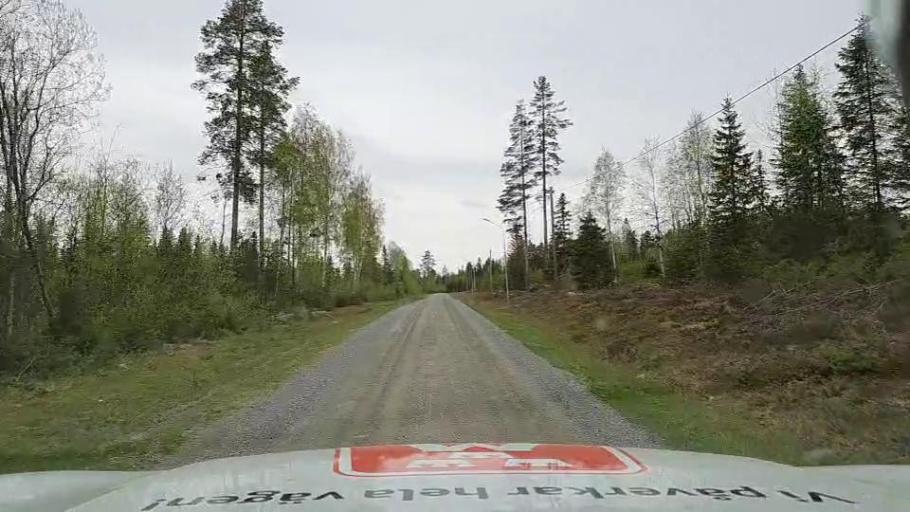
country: SE
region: Jaemtland
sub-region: Bergs Kommun
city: Hoverberg
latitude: 62.5641
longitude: 14.6772
